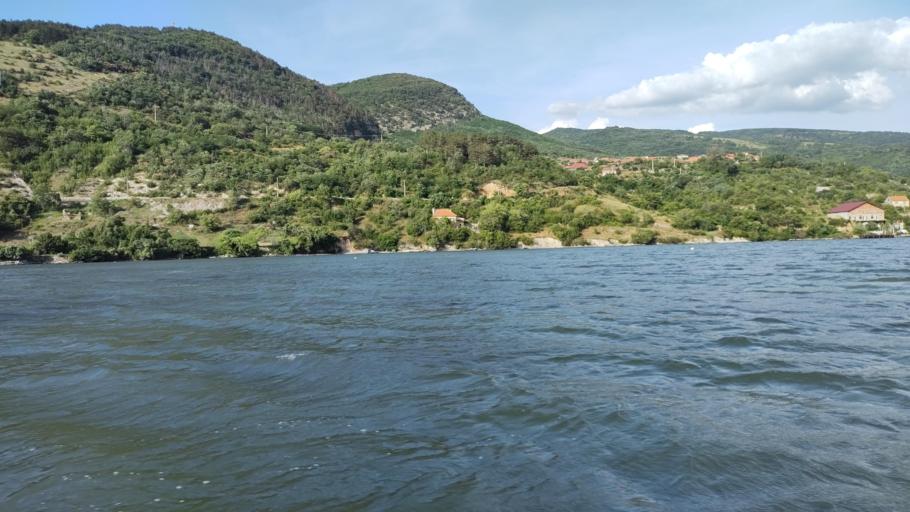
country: RO
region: Mehedinti
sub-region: Comuna Svinita
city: Svinita
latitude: 44.4991
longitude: 22.0902
